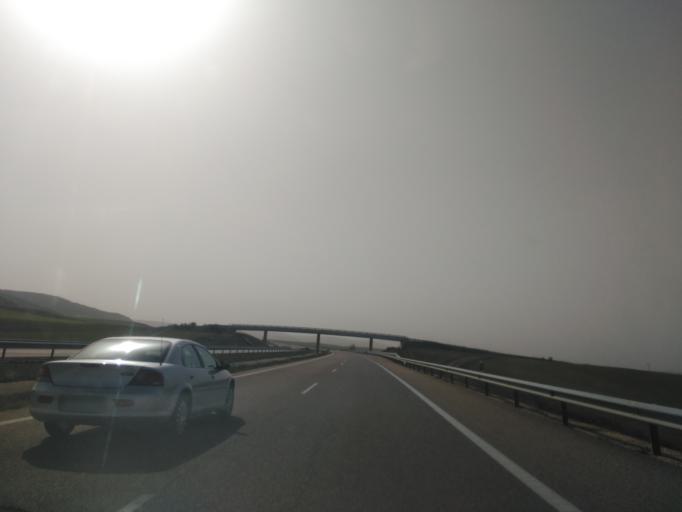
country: ES
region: Castille and Leon
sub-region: Provincia de Palencia
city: Amusco
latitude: 42.1585
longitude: -4.4671
